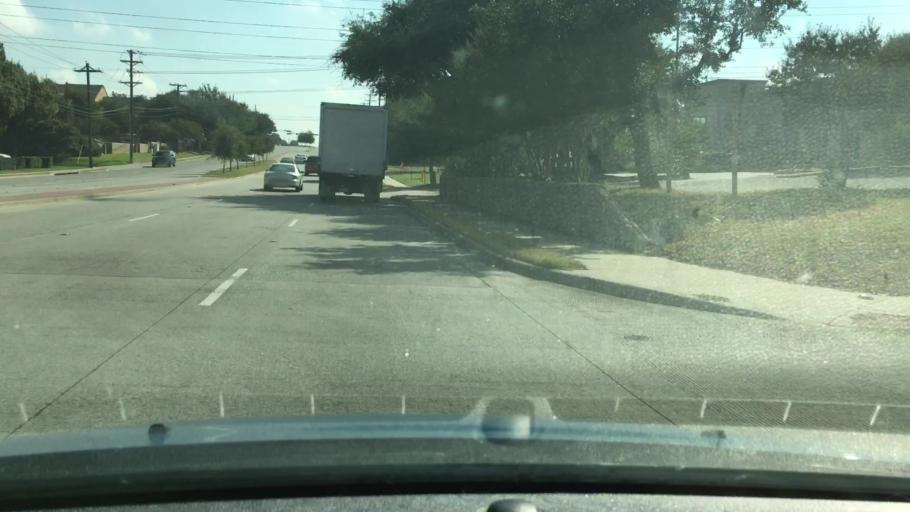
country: US
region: Texas
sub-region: Dallas County
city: Addison
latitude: 32.9870
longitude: -96.8515
